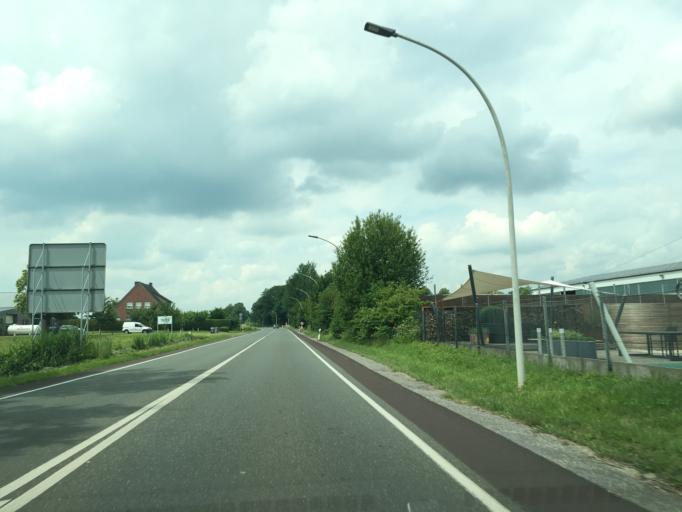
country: DE
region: North Rhine-Westphalia
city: Emsdetten
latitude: 52.1749
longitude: 7.4975
